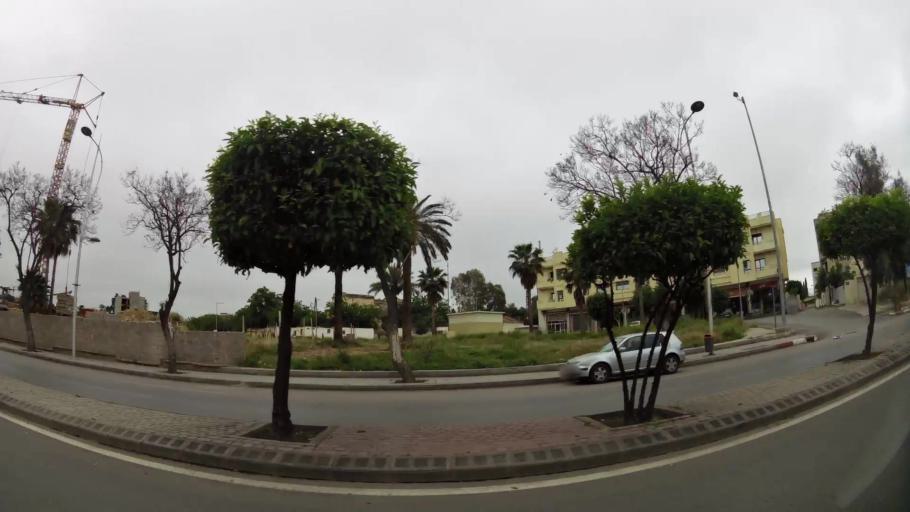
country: MA
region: Fes-Boulemane
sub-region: Fes
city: Fes
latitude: 34.0280
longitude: -4.9985
